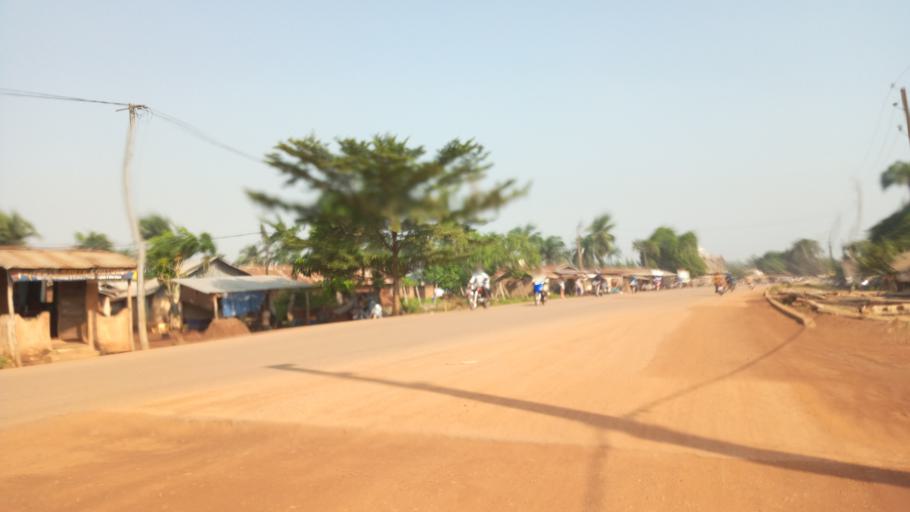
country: BJ
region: Queme
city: Porto-Novo
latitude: 6.5316
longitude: 2.6485
